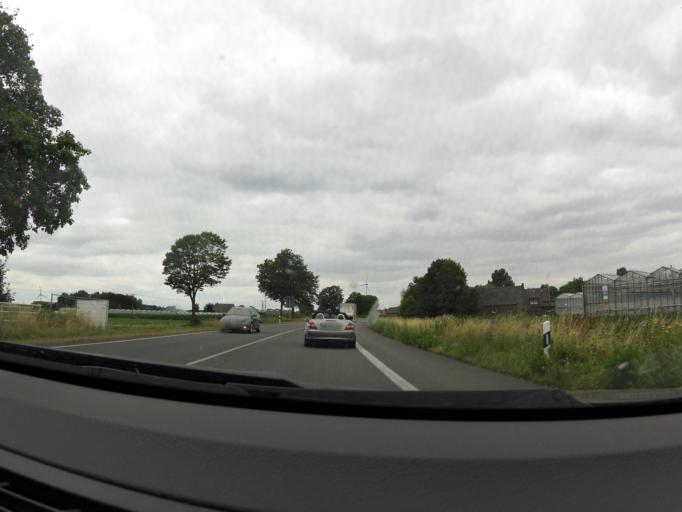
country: DE
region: North Rhine-Westphalia
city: Straelen
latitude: 51.4537
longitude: 6.2735
